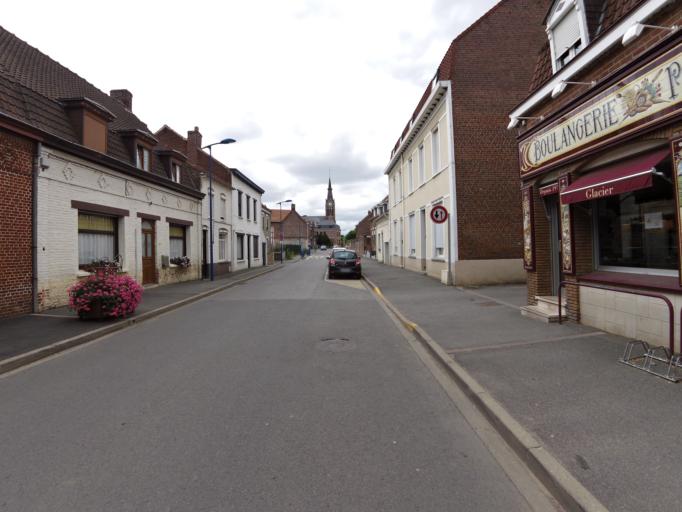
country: FR
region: Nord-Pas-de-Calais
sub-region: Departement du Nord
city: Godewaersvelde
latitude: 50.7955
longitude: 2.6454
